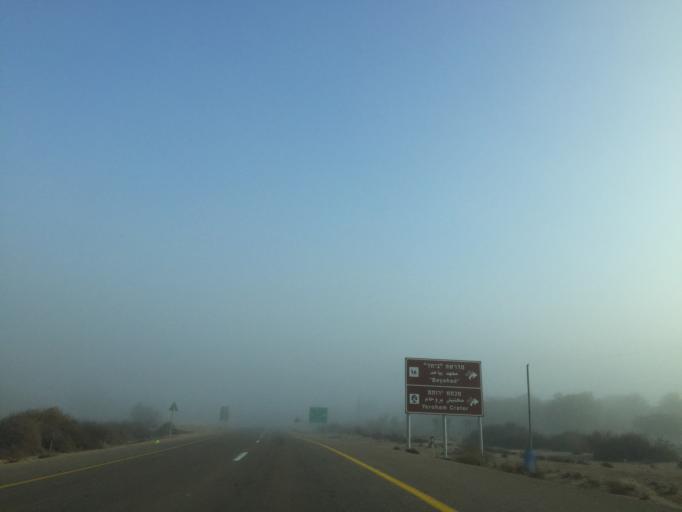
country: IL
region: Southern District
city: Yeroham
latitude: 30.9874
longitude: 34.9100
